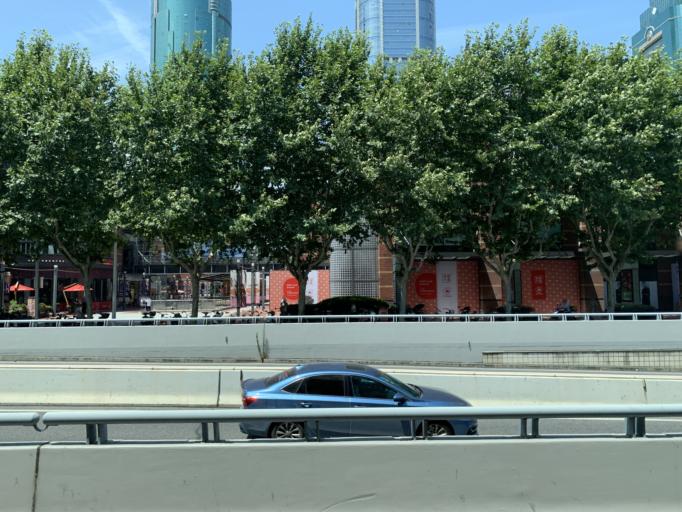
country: CN
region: Shanghai Shi
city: Pudong
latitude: 31.2301
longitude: 121.5214
